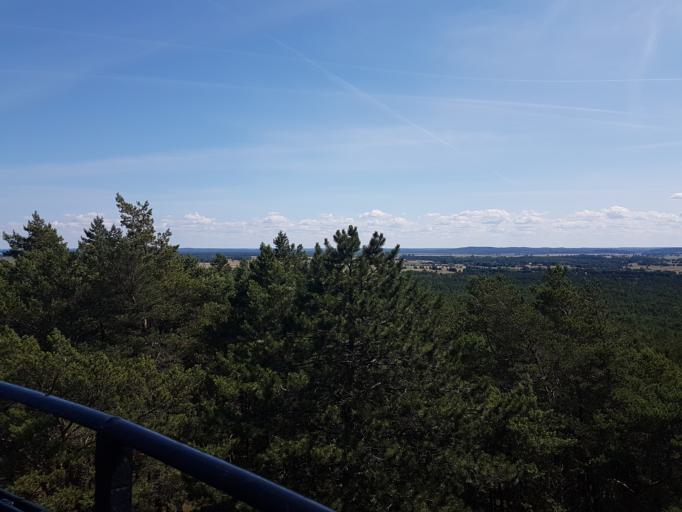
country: PL
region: Pomeranian Voivodeship
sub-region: Powiat slupski
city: Smoldzino
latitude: 54.7183
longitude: 17.2412
